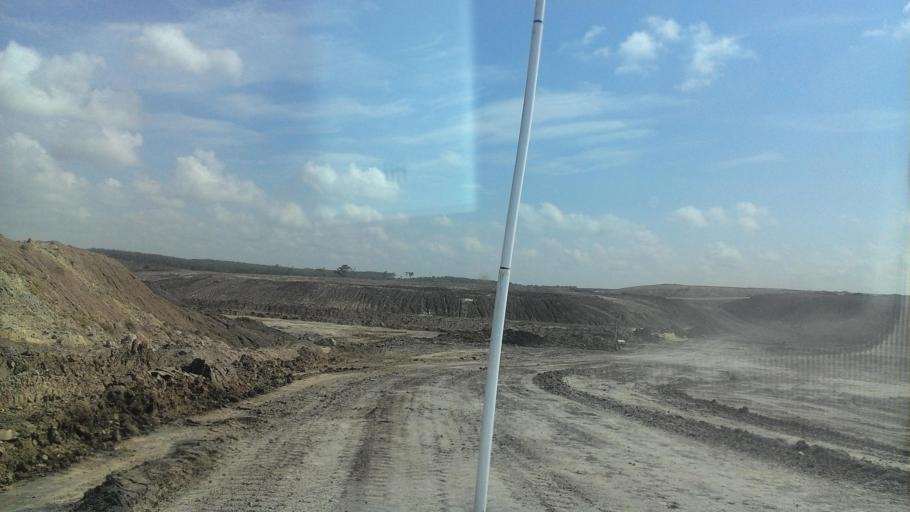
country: ID
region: South Kalimantan
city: Tanta
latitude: -2.1804
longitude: 115.4675
